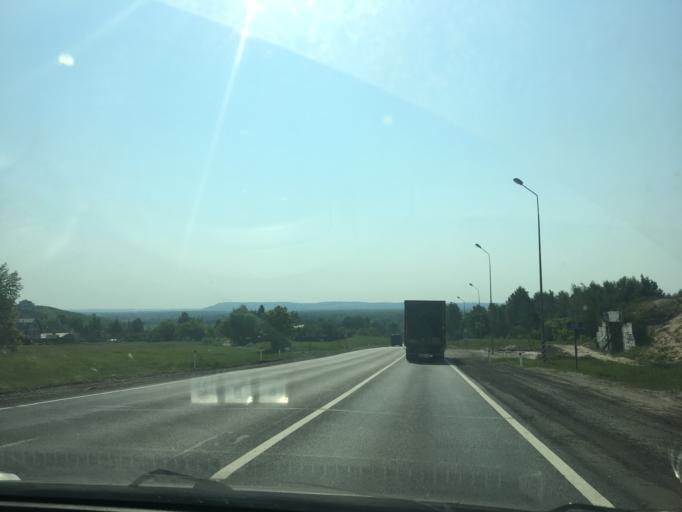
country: RU
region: Nizjnij Novgorod
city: Kstovo
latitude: 56.1032
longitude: 44.2967
